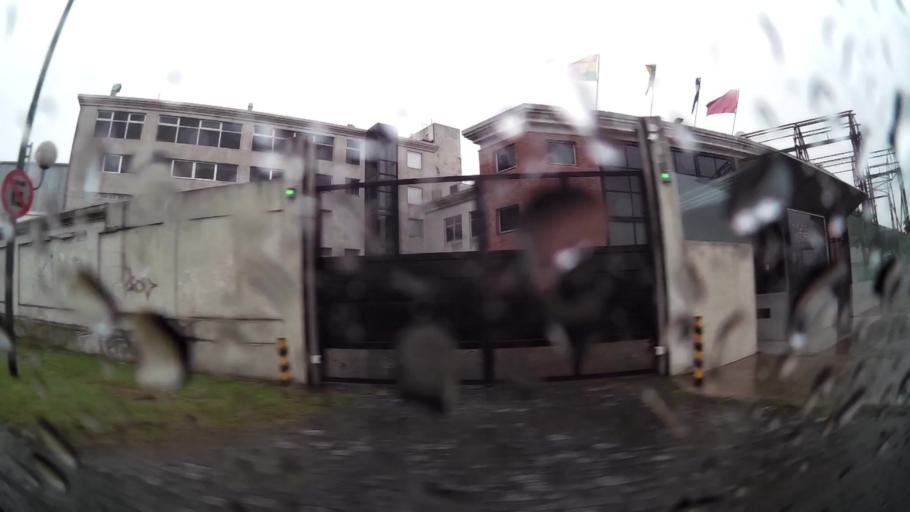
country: AR
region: Buenos Aires
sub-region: Partido de Avellaneda
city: Avellaneda
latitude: -34.6441
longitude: -58.3576
